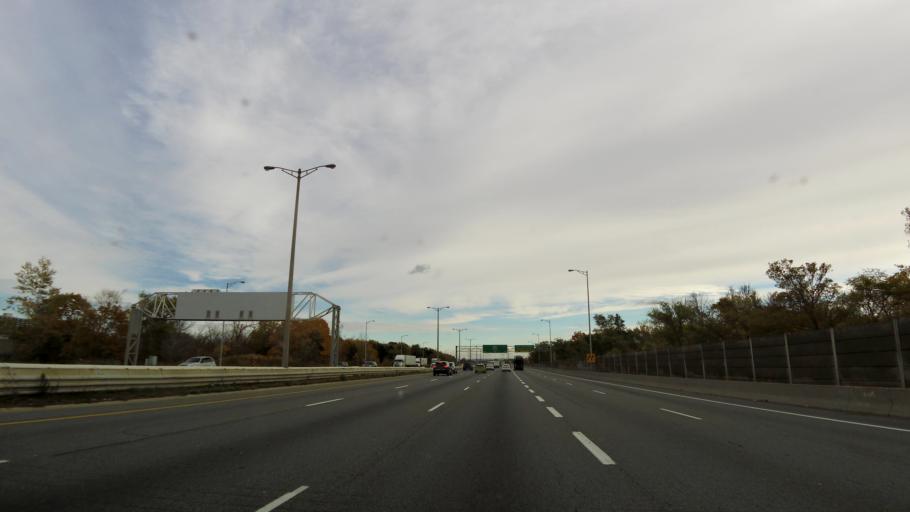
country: CA
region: Ontario
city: Burlington
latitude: 43.3204
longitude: -79.8160
